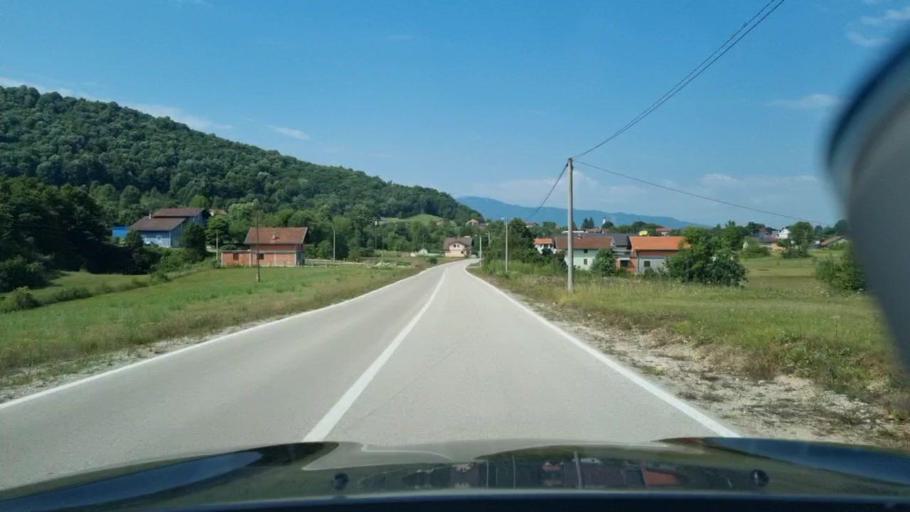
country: BA
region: Federation of Bosnia and Herzegovina
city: Ostrozac
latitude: 44.8817
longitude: 15.9179
